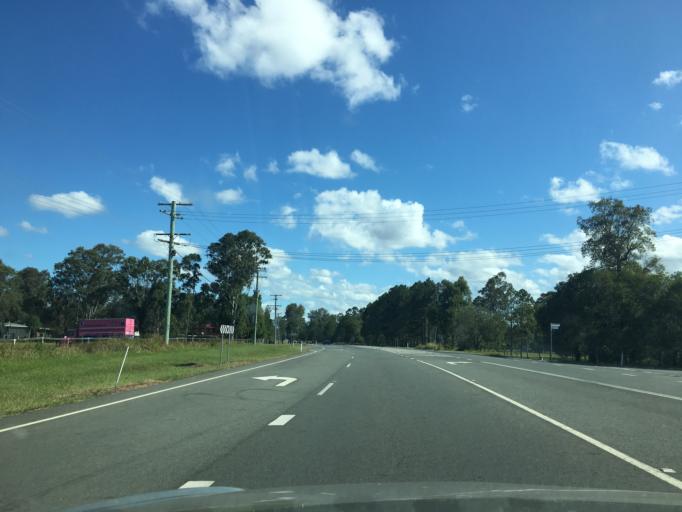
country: AU
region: Queensland
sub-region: Logan
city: Waterford West
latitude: -27.7148
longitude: 153.1294
